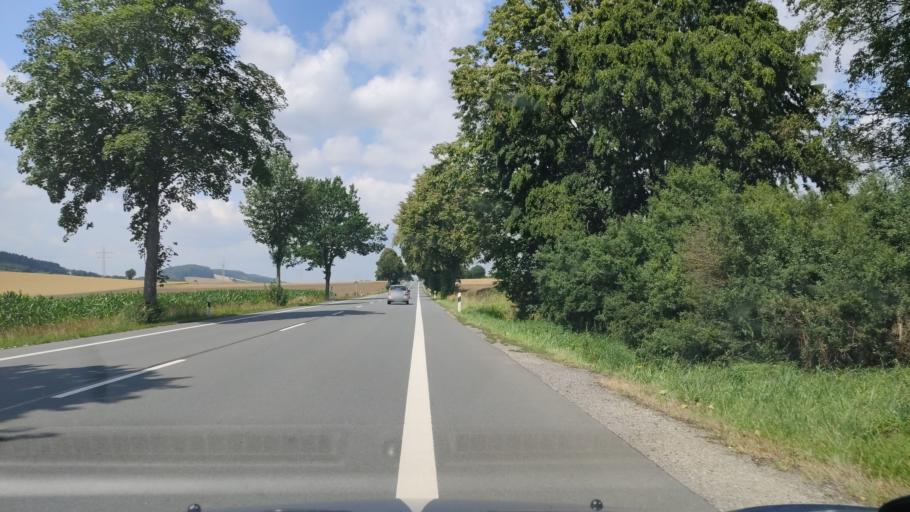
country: DE
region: Lower Saxony
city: Dielmissen
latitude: 51.9560
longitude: 9.6097
